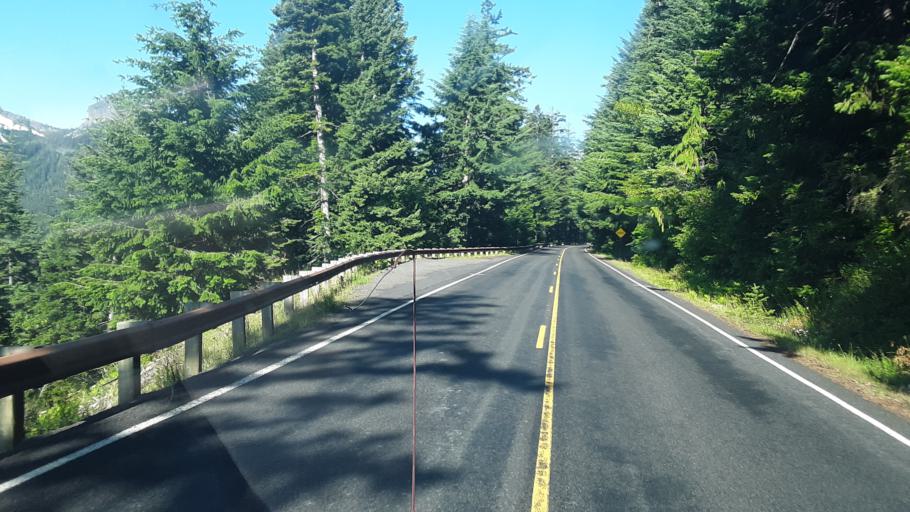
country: US
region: Washington
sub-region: Kittitas County
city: Cle Elum
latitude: 46.8974
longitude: -121.4499
